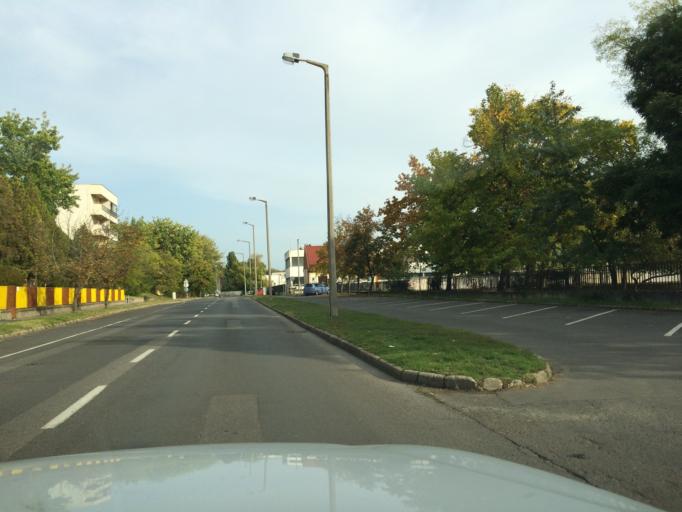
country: HU
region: Szabolcs-Szatmar-Bereg
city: Nyiregyhaza
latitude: 47.9677
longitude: 21.7192
